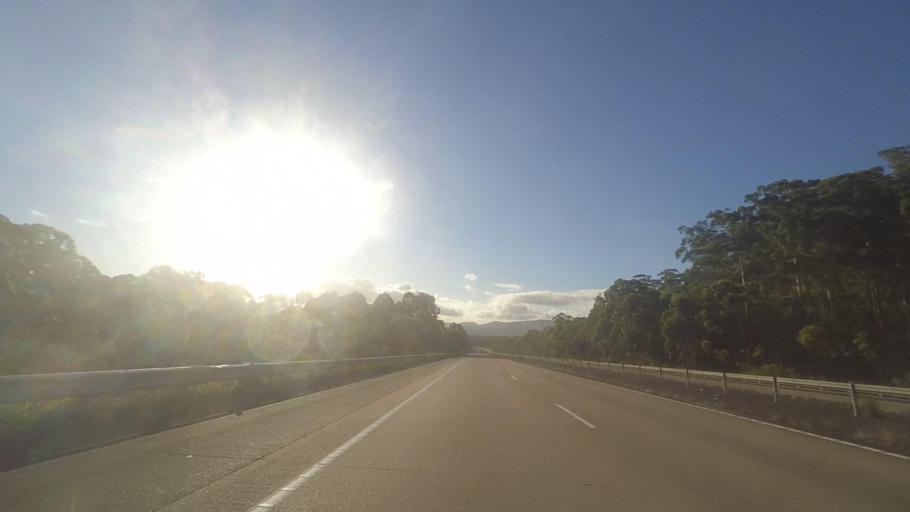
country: AU
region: New South Wales
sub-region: Great Lakes
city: Bulahdelah
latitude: -32.3874
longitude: 152.2423
